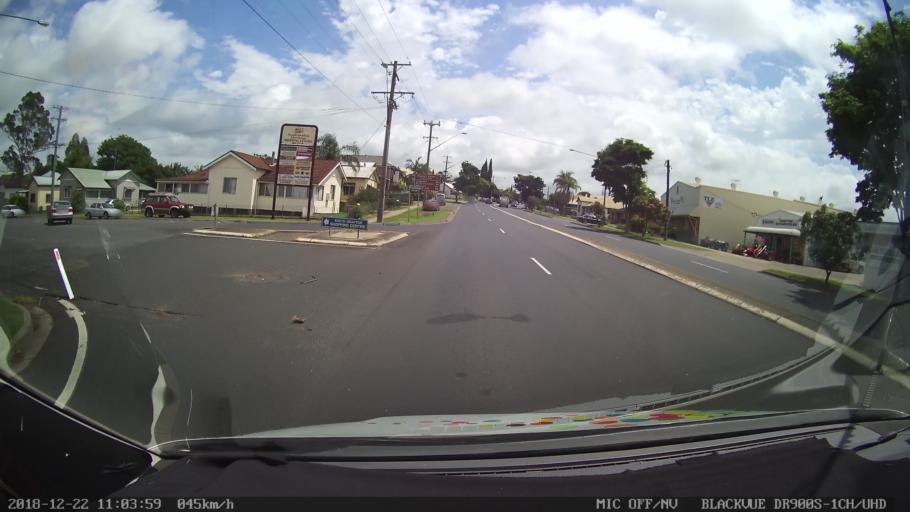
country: AU
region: New South Wales
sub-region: Clarence Valley
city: South Grafton
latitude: -29.7056
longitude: 152.9397
